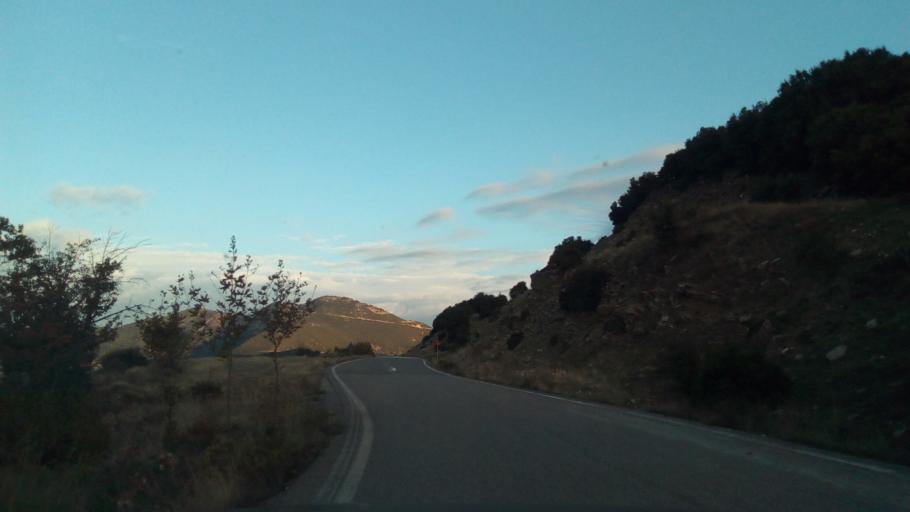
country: GR
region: West Greece
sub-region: Nomos Aitolias kai Akarnanias
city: Nafpaktos
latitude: 38.5071
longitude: 21.8351
